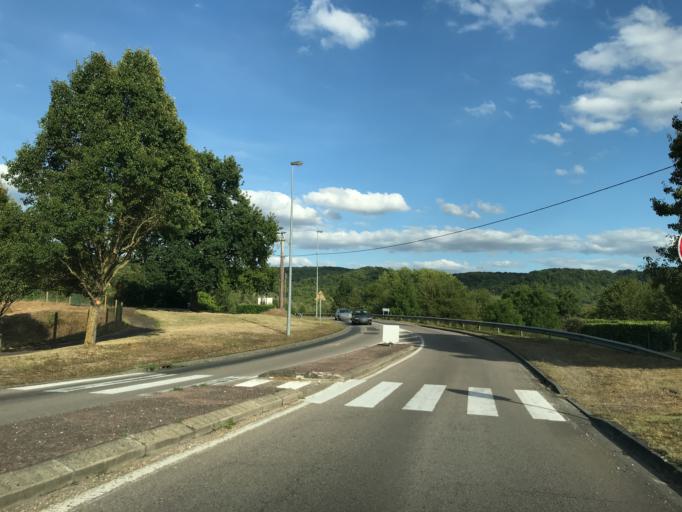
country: FR
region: Haute-Normandie
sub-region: Departement de l'Eure
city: Les Andelys
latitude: 49.2335
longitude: 1.3863
